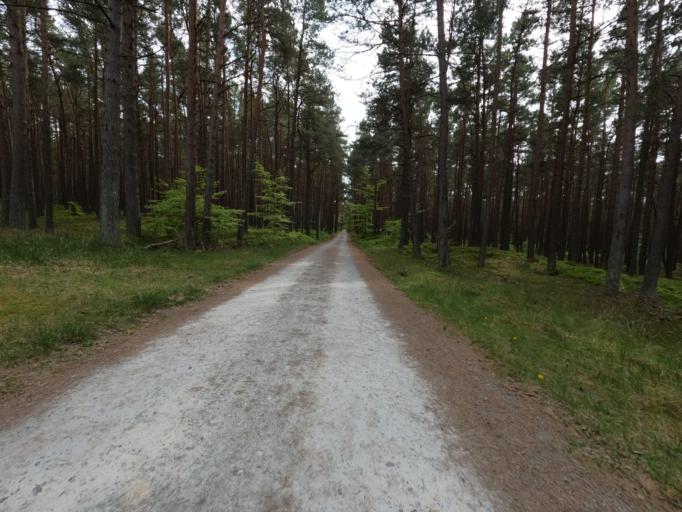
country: DE
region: Mecklenburg-Vorpommern
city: Ostseebad Prerow
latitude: 54.4607
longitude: 12.5143
